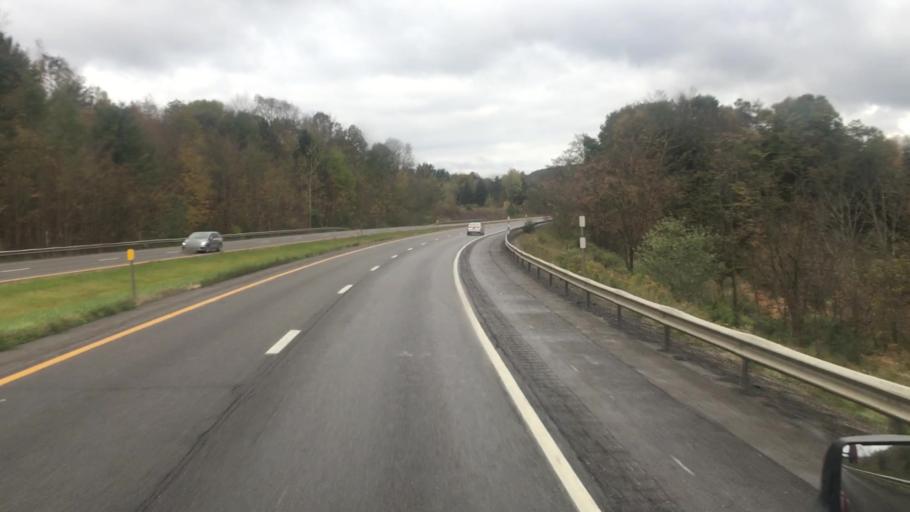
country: US
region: New York
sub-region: Broome County
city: Chenango Bridge
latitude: 42.1578
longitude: -75.8072
